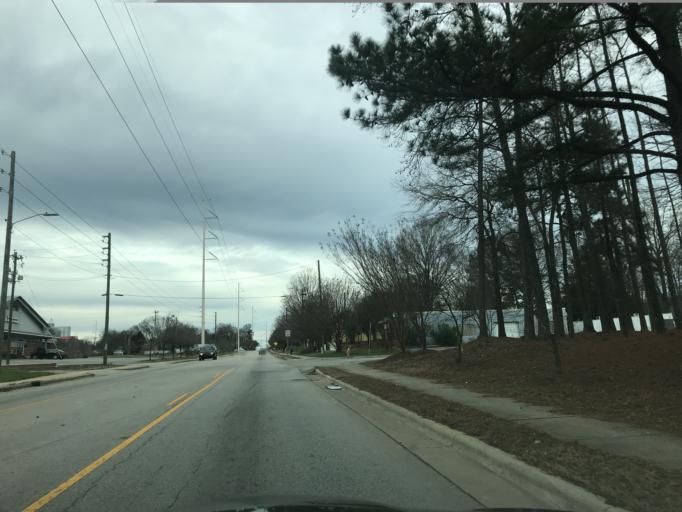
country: US
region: North Carolina
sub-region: Wake County
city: Raleigh
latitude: 35.7600
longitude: -78.6313
